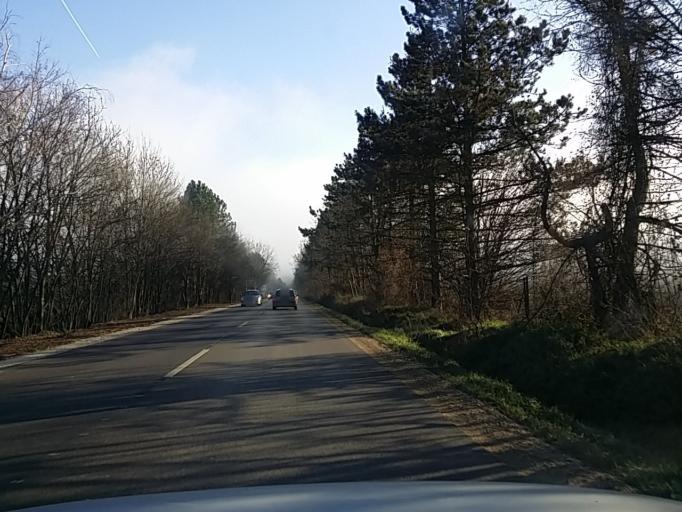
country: HU
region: Pest
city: Solymar
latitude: 47.5529
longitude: 18.9298
